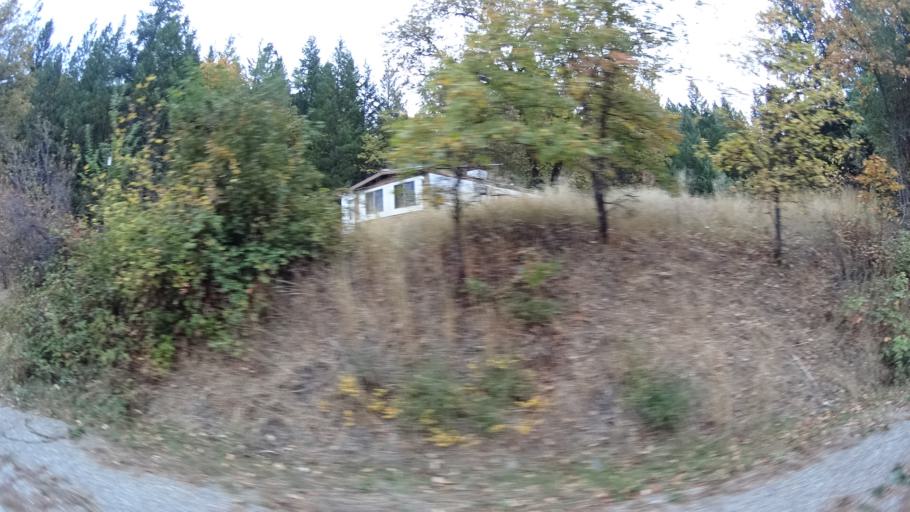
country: US
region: California
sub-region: Siskiyou County
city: Happy Camp
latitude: 41.8823
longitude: -123.4225
